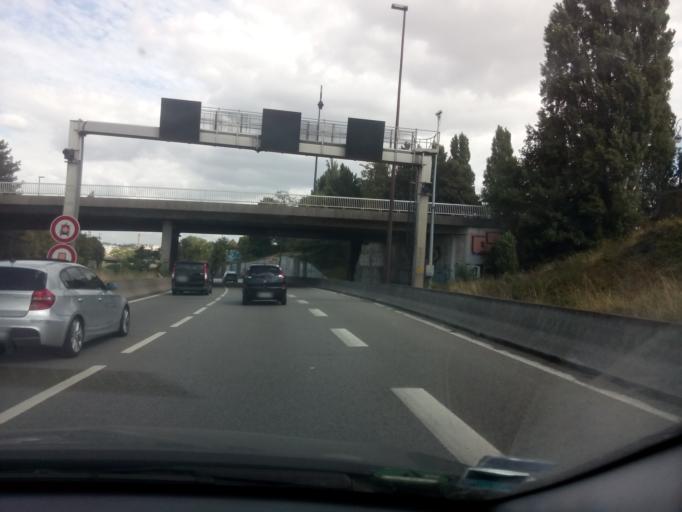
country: FR
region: Ile-de-France
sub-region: Departement des Hauts-de-Seine
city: Antony
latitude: 48.7602
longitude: 2.2901
